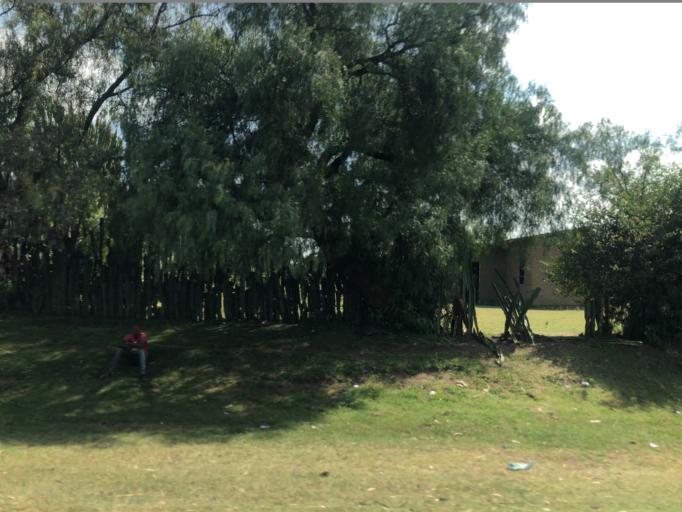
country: ET
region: Oromiya
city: Shashemene
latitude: 7.2297
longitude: 38.6321
